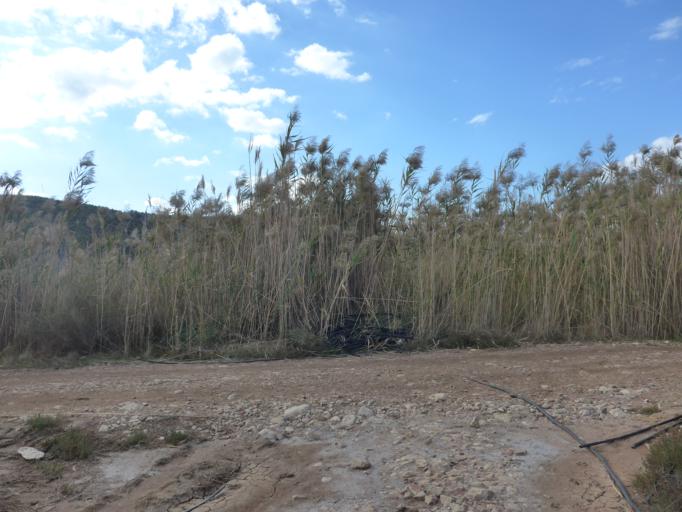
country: GR
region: Peloponnese
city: Asklipieio
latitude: 37.4763
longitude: 23.0045
